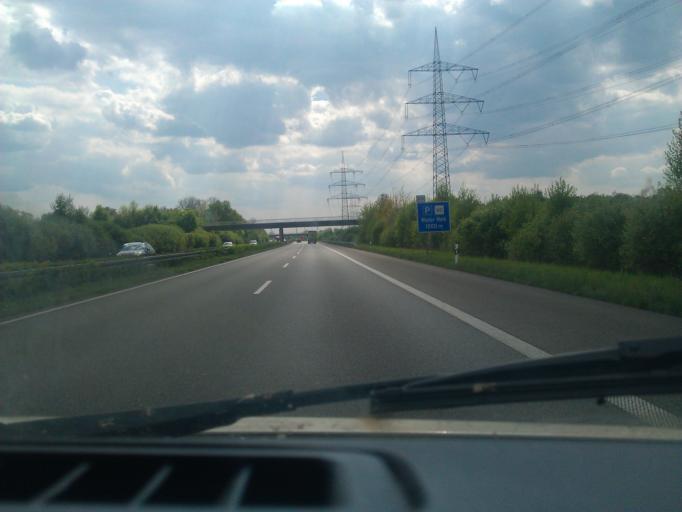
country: DE
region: North Rhine-Westphalia
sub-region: Regierungsbezirk Munster
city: Ochtrup
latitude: 52.2352
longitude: 7.1508
